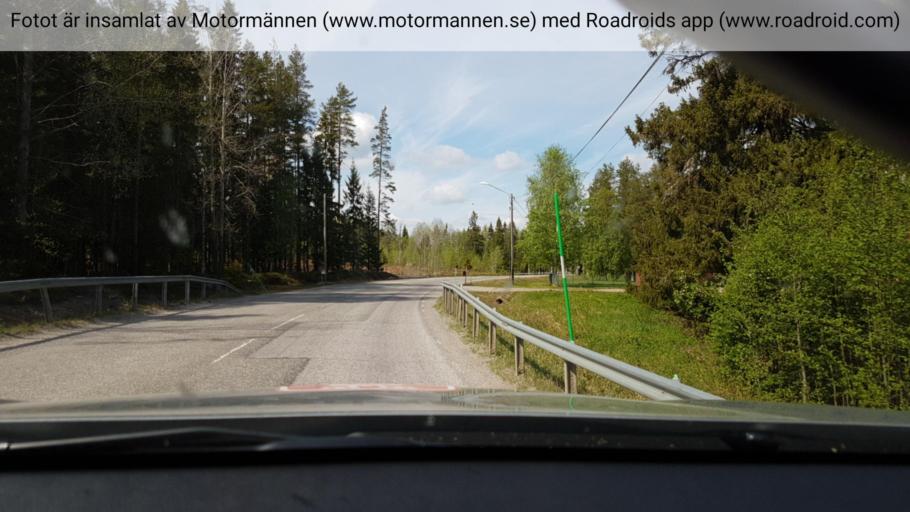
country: SE
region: Vaesterbotten
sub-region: Umea Kommun
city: Roback
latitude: 63.8576
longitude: 20.0780
